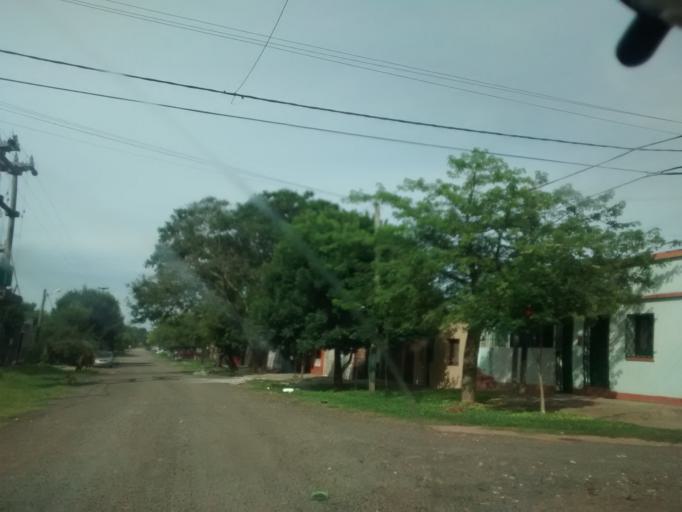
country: AR
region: Chaco
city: Resistencia
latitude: -27.4369
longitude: -58.9921
